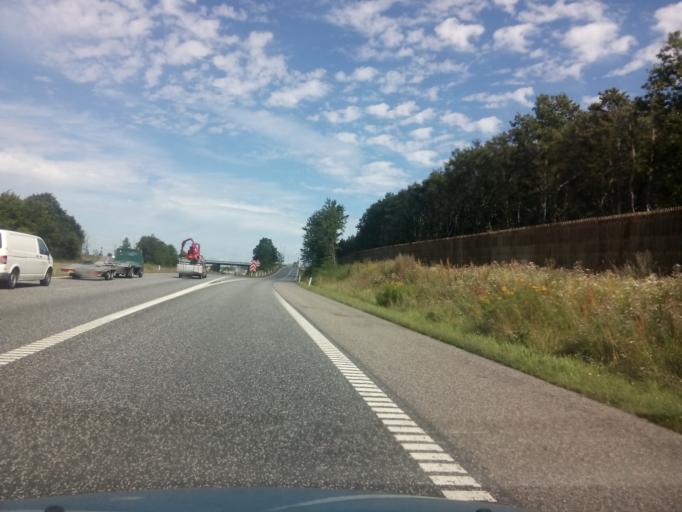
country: DK
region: Central Jutland
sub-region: Randers Kommune
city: Randers
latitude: 56.4649
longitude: 9.9859
